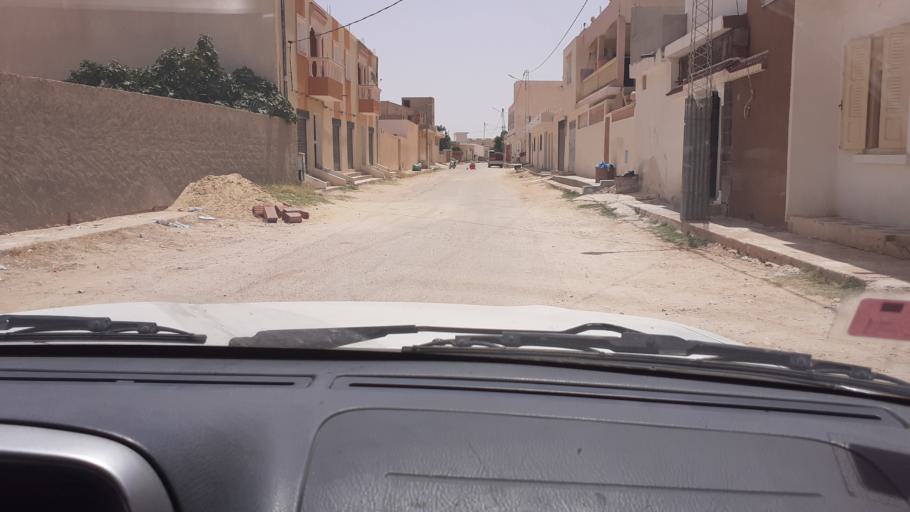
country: TN
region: Qabis
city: Matmata
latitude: 33.6143
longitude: 10.2862
